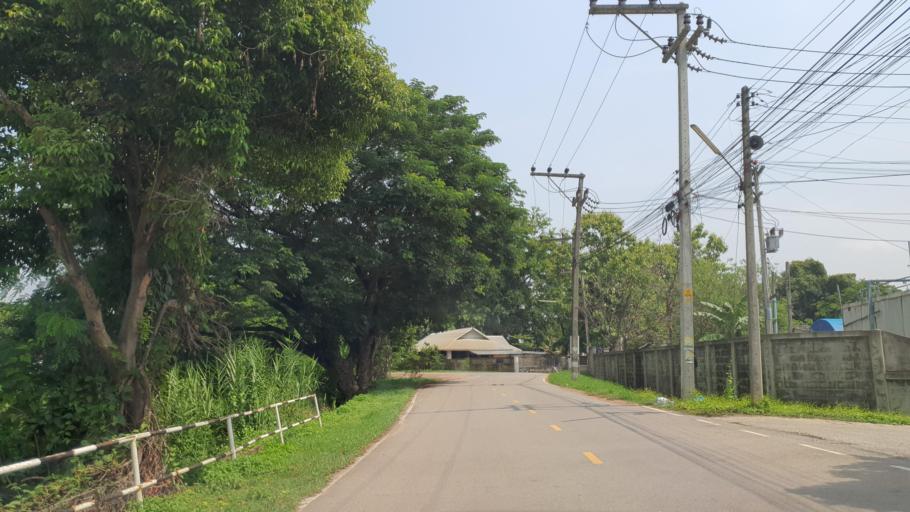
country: TH
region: Lamphun
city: Lamphun
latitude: 18.6053
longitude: 99.0265
